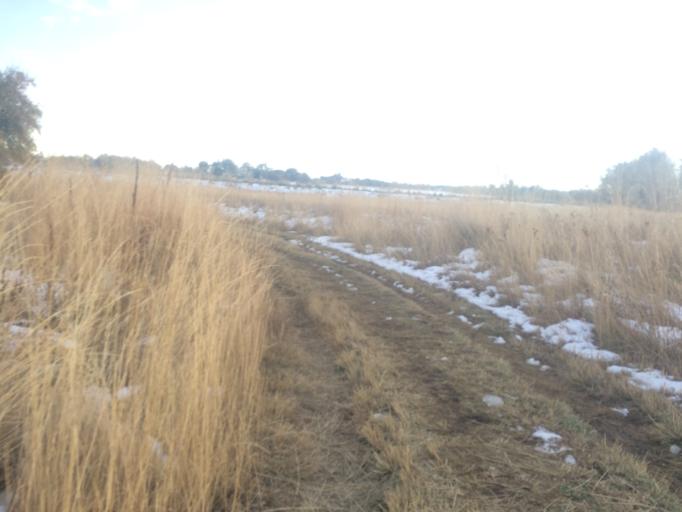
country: US
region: Colorado
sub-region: Boulder County
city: Gunbarrel
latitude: 40.0226
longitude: -105.1534
